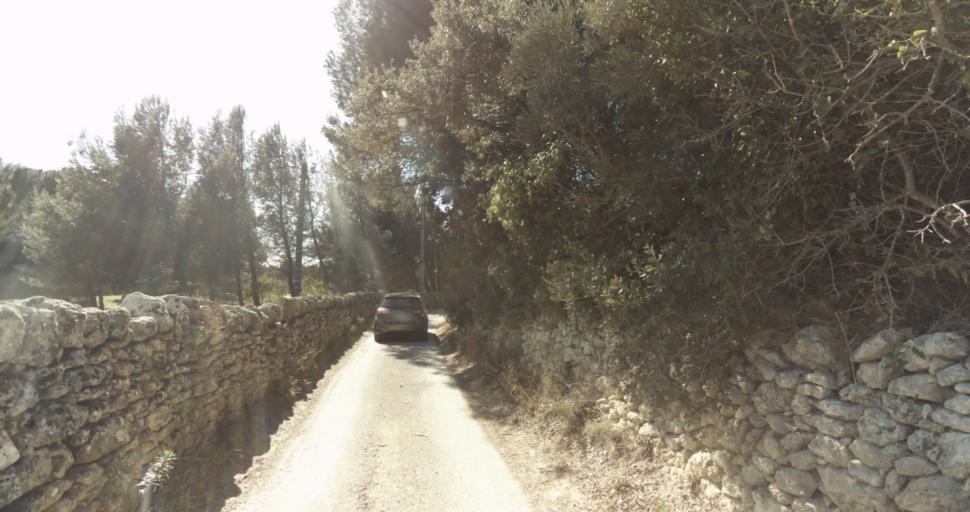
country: FR
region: Provence-Alpes-Cote d'Azur
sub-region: Departement des Bouches-du-Rhone
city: Pelissanne
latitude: 43.6437
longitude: 5.1687
